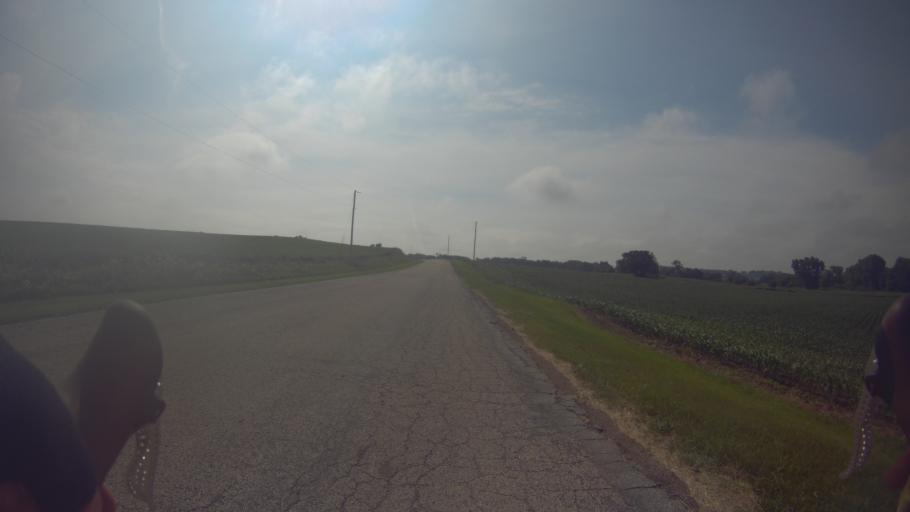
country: US
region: Wisconsin
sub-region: Dane County
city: Stoughton
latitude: 42.9805
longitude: -89.1896
